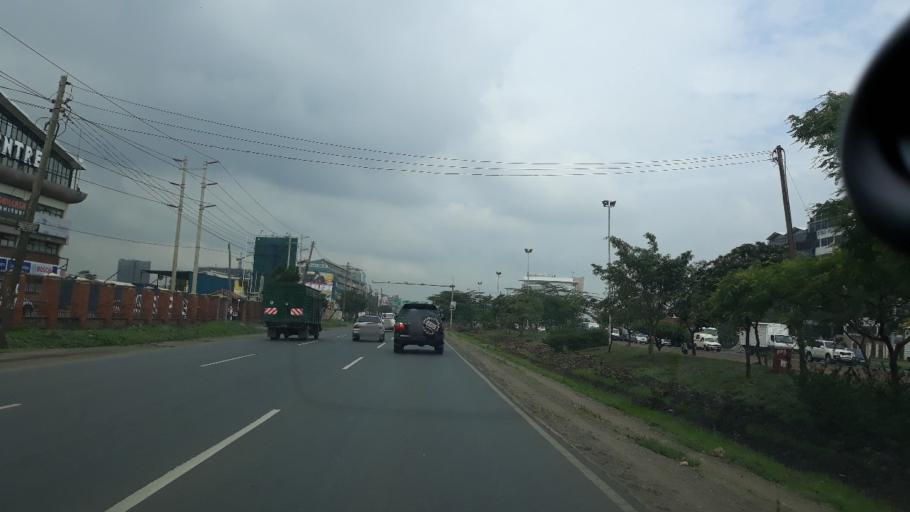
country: KE
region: Nairobi Area
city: Pumwani
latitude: -1.3287
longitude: 36.8534
